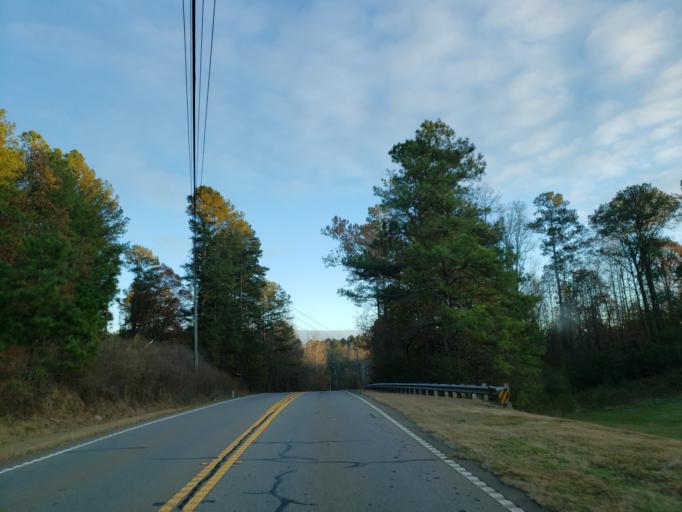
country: US
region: Georgia
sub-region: Cherokee County
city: Ball Ground
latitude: 34.2666
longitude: -84.2901
